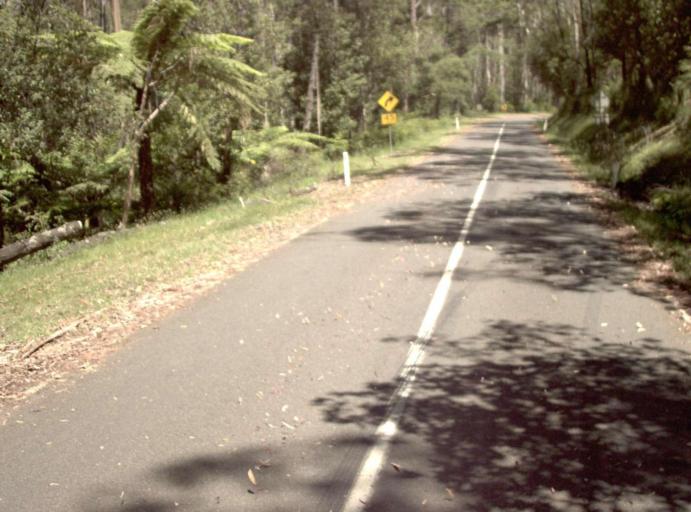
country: AU
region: Victoria
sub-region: Yarra Ranges
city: Millgrove
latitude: -37.7403
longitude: 145.7208
